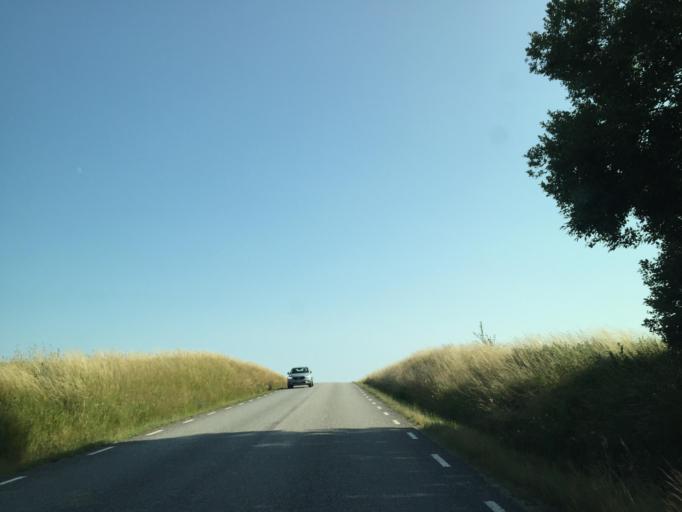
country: SE
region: Vaestra Goetaland
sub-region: Lilla Edets Kommun
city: Lilla Edet
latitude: 58.1944
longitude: 12.1177
